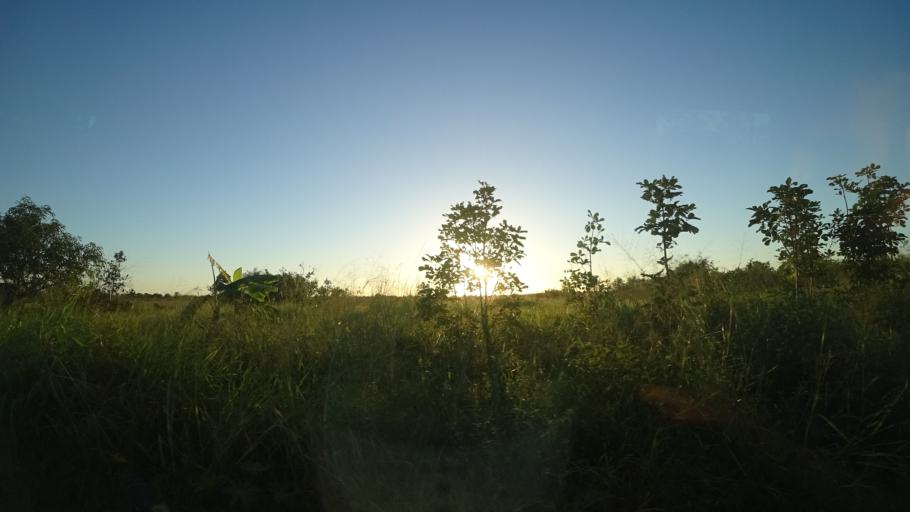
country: MZ
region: Sofala
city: Beira
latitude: -19.6503
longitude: 35.0582
